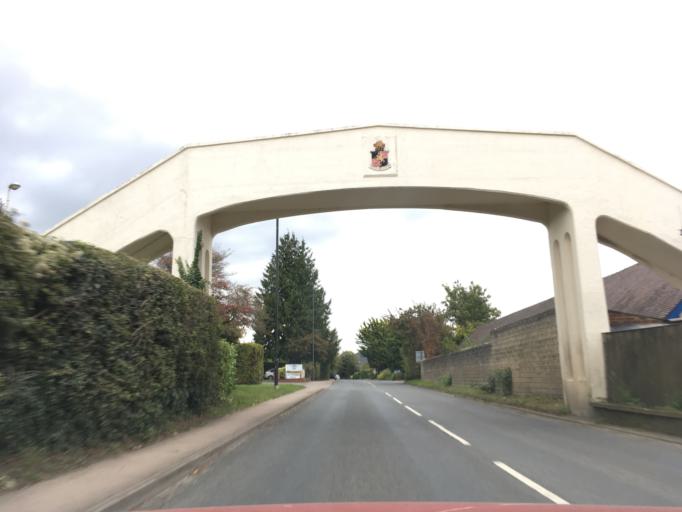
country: GB
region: England
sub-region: Gloucestershire
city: Stonehouse
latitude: 51.7411
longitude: -2.2705
